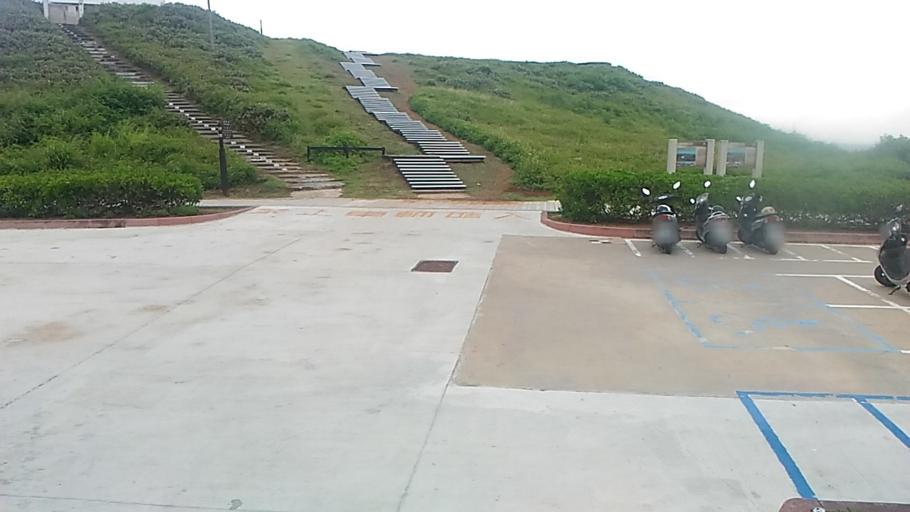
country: TW
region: Taiwan
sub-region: Penghu
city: Ma-kung
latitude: 23.3806
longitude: 119.4950
